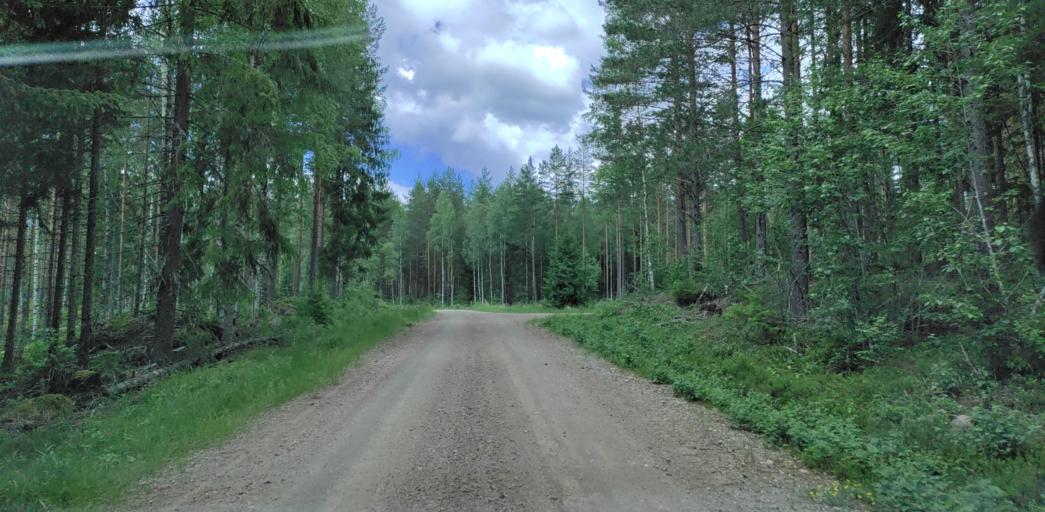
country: SE
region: Vaermland
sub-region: Hagfors Kommun
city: Ekshaerad
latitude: 60.0926
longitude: 13.4082
